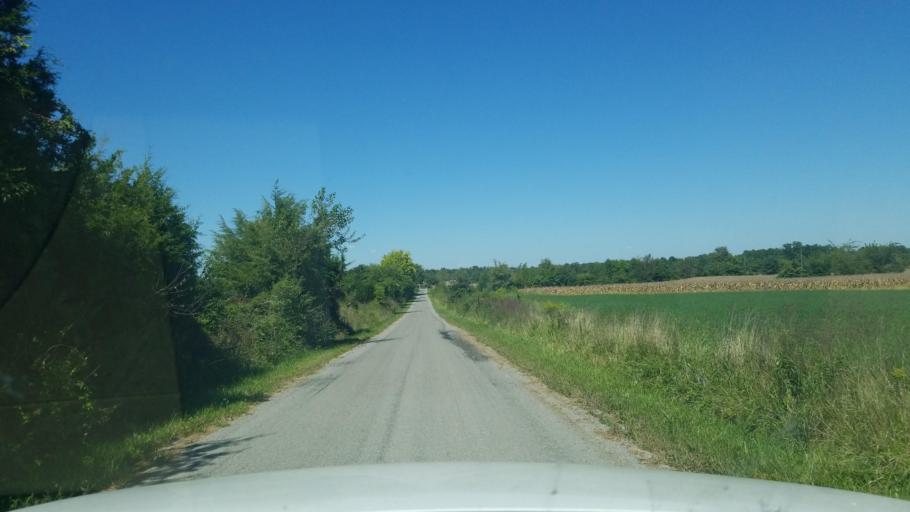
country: US
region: Illinois
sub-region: Saline County
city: Eldorado
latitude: 37.8572
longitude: -88.5119
